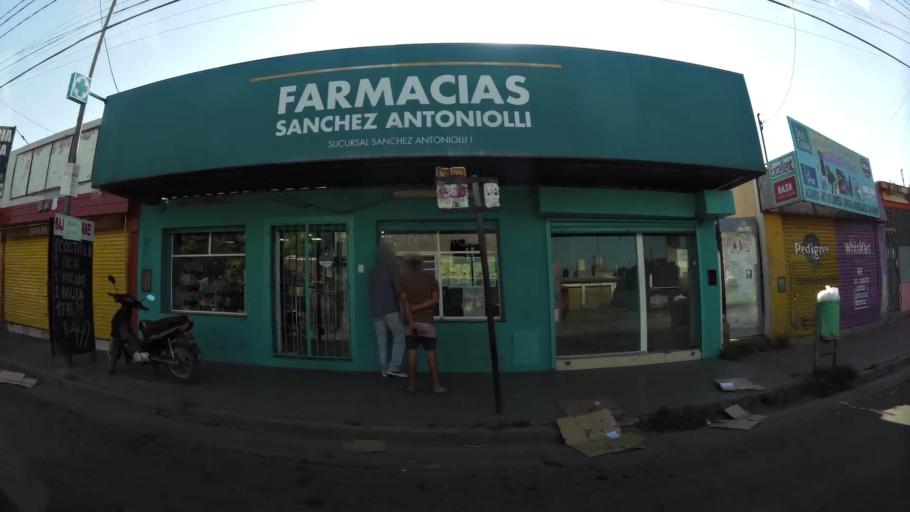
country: AR
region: Cordoba
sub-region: Departamento de Capital
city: Cordoba
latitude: -31.4743
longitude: -64.2252
